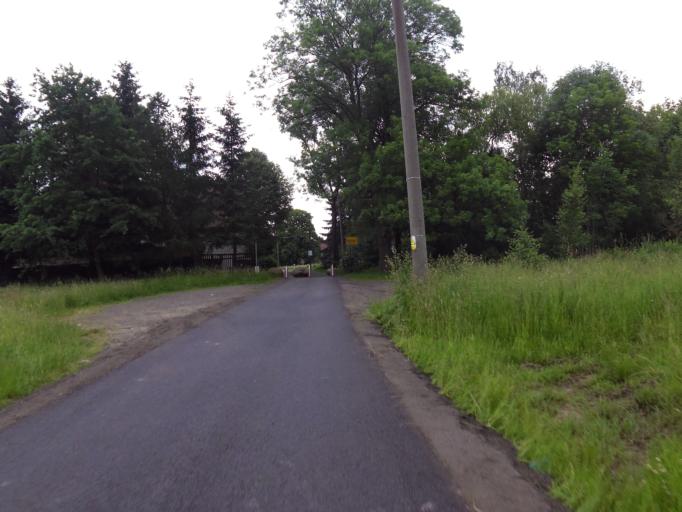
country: CZ
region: Ustecky
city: Varnsdorf
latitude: 50.8811
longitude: 14.6294
